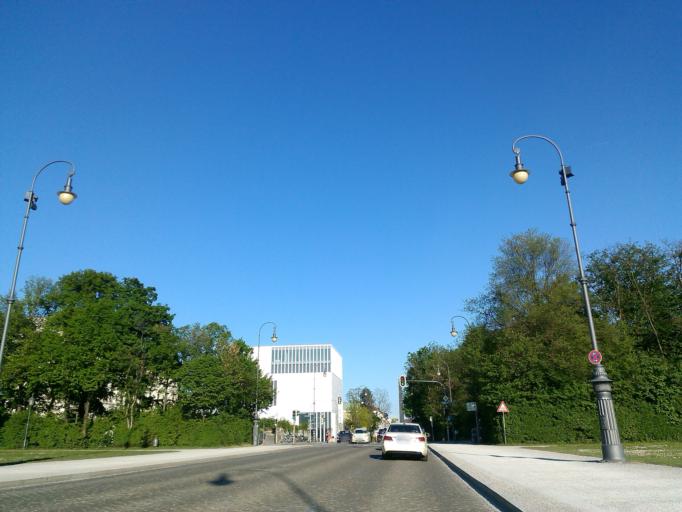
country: DE
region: Bavaria
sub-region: Upper Bavaria
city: Munich
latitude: 48.1457
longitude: 11.5657
